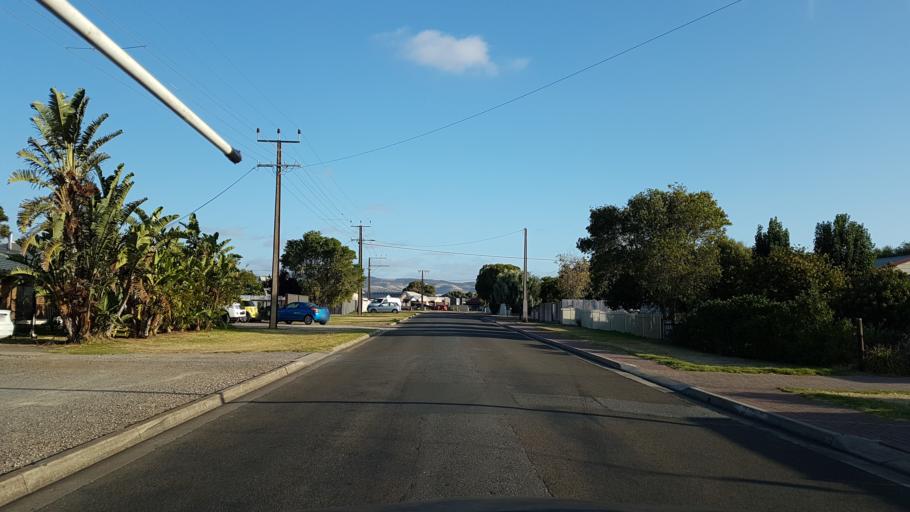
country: AU
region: South Australia
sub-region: Onkaparinga
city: Port Willunga
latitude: -35.2769
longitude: 138.4520
